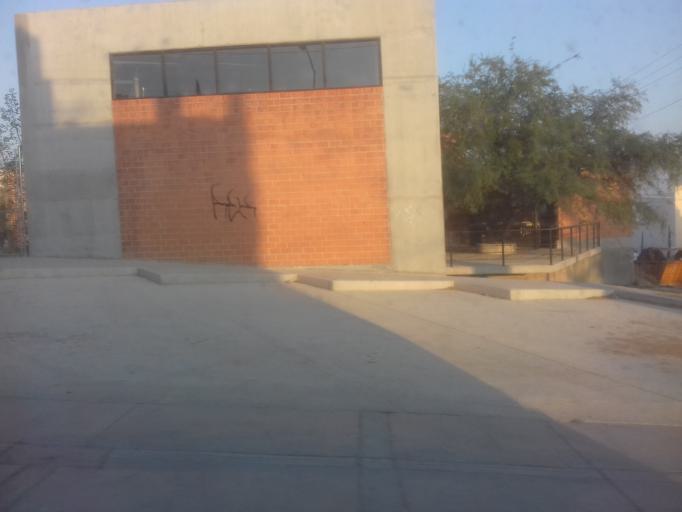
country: MX
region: Aguascalientes
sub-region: Aguascalientes
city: San Sebastian [Fraccionamiento]
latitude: 21.8465
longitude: -102.2620
